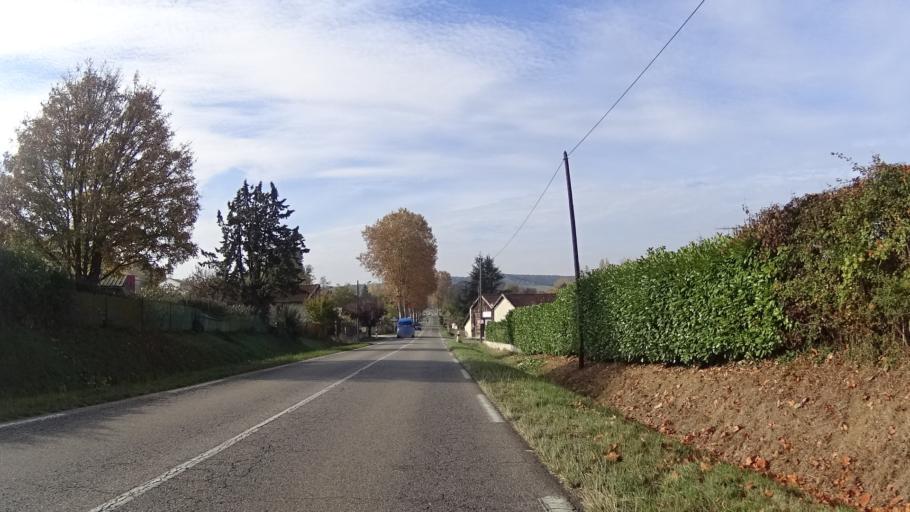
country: FR
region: Aquitaine
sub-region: Departement du Lot-et-Garonne
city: Roquefort
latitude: 44.1742
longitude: 0.5575
